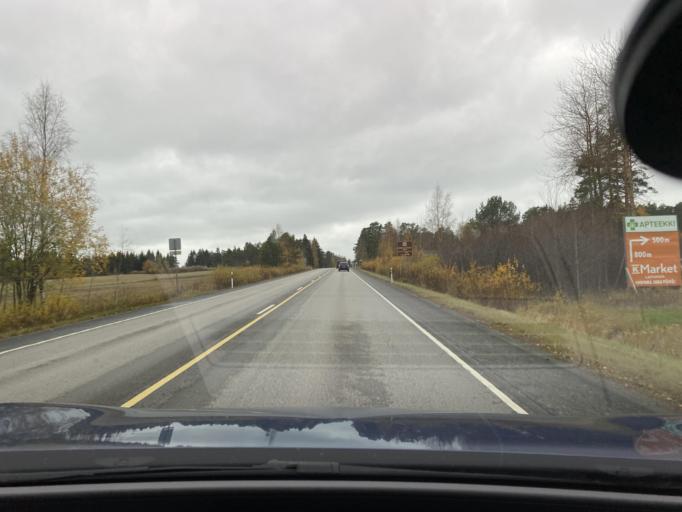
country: FI
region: Satakunta
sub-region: Rauma
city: Lappi
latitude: 61.0992
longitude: 21.8635
